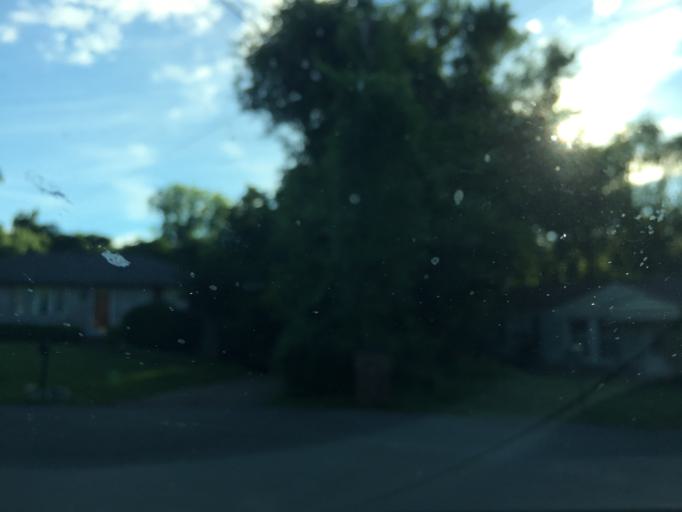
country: US
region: Tennessee
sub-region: Davidson County
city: Oak Hill
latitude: 36.0655
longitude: -86.7246
